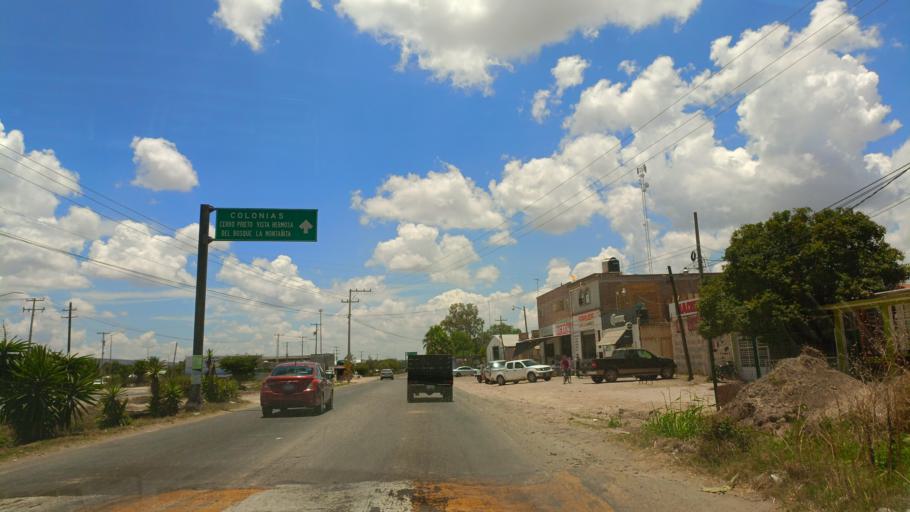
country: MX
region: Guanajuato
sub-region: San Luis de la Paz
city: San Ignacio
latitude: 21.2873
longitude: -100.5572
